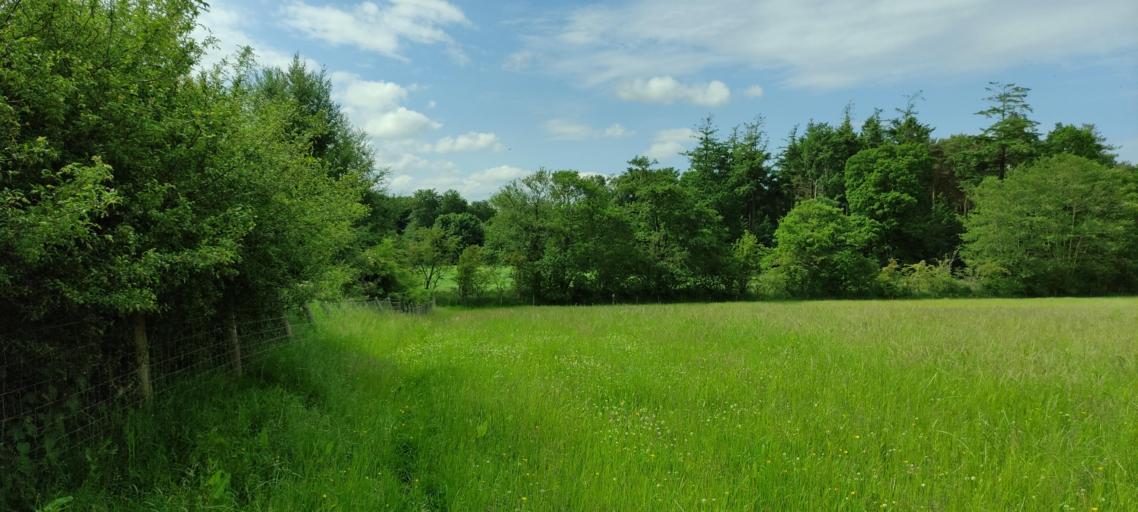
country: GB
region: England
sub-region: Cumbria
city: Cockermouth
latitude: 54.6849
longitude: -3.3879
